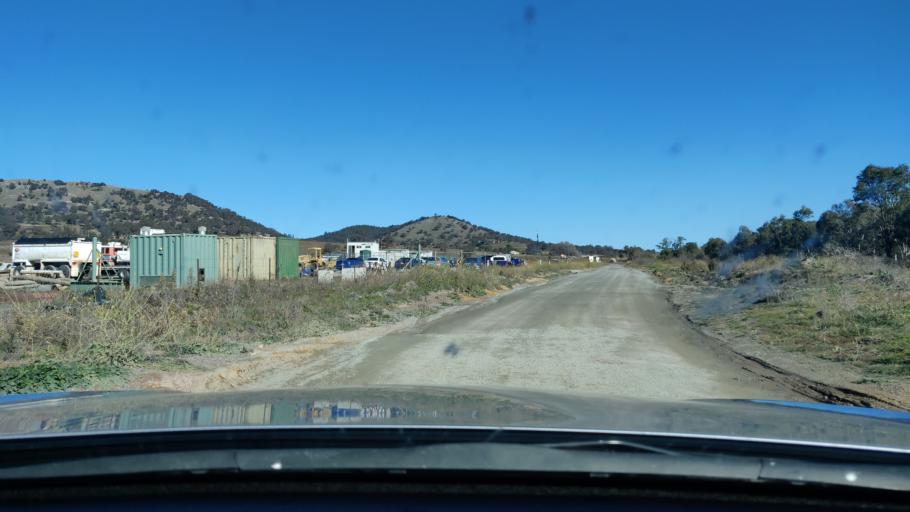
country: AU
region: Australian Capital Territory
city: Macarthur
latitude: -35.4019
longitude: 149.1635
